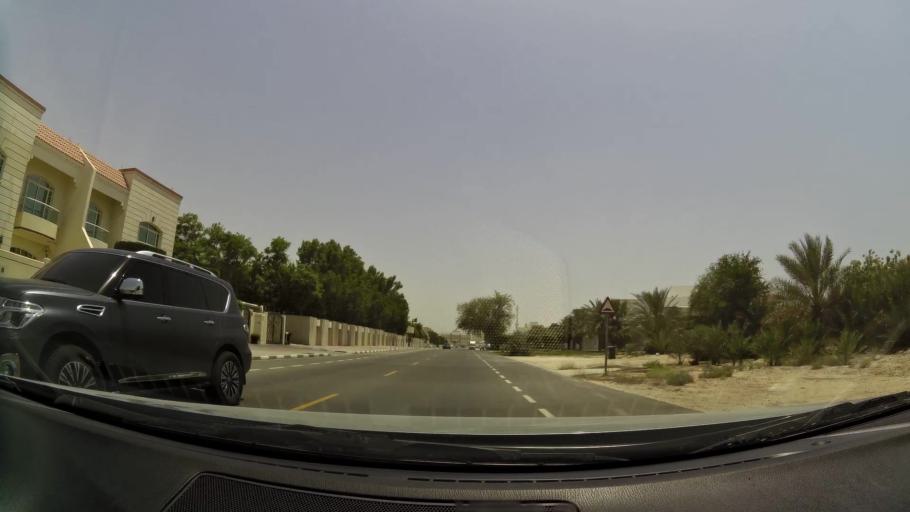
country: AE
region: Dubai
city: Dubai
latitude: 25.1586
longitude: 55.2149
